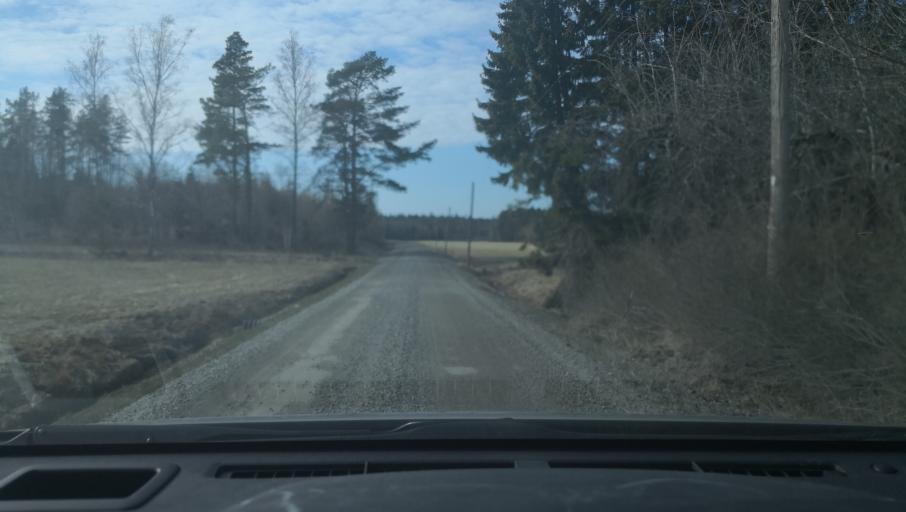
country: SE
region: Uppsala
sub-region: Heby Kommun
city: Heby
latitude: 59.8472
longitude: 16.8927
